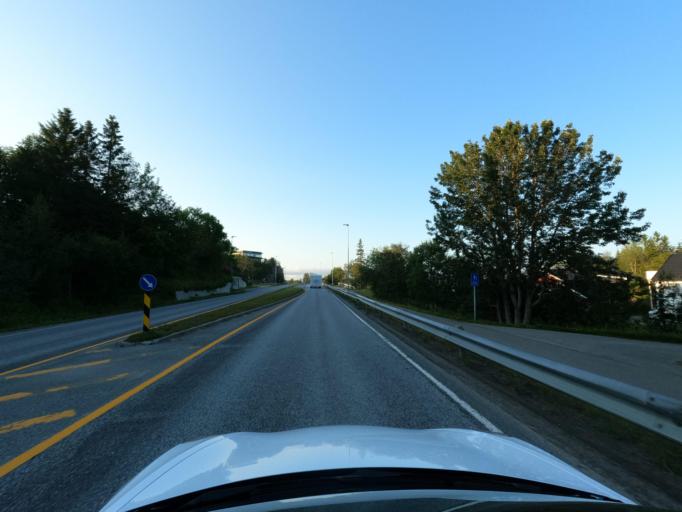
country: NO
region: Troms
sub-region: Harstad
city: Harstad
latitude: 68.7555
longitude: 16.5664
